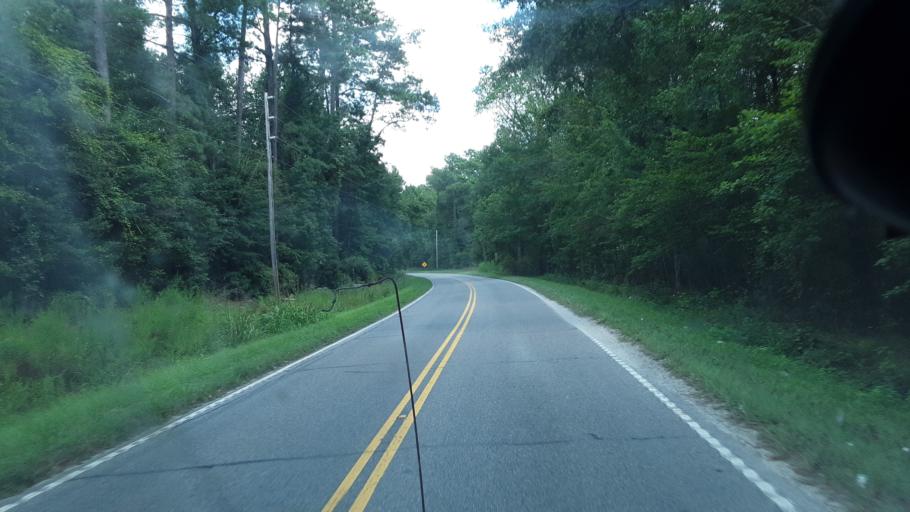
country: US
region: South Carolina
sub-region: Florence County
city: Johnsonville
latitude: 33.6592
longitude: -79.4183
